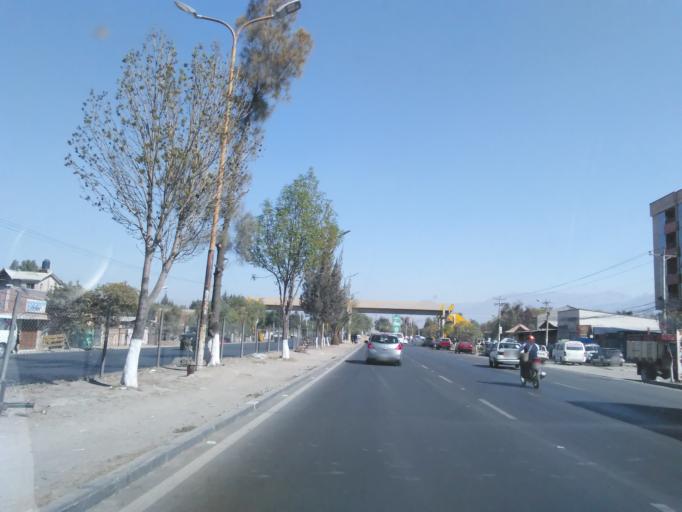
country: BO
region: Cochabamba
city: Cochabamba
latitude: -17.3908
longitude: -66.2423
